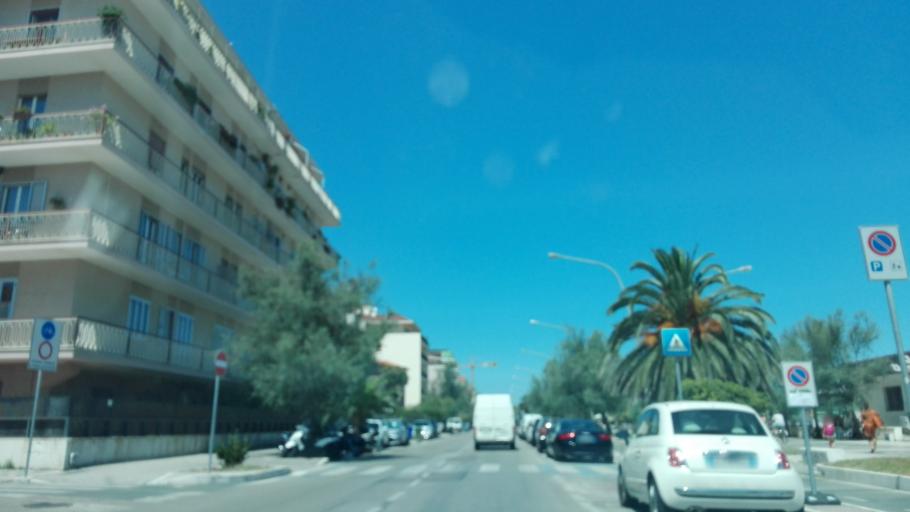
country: IT
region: Abruzzo
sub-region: Provincia di Pescara
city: Pescara
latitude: 42.4785
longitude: 14.2039
